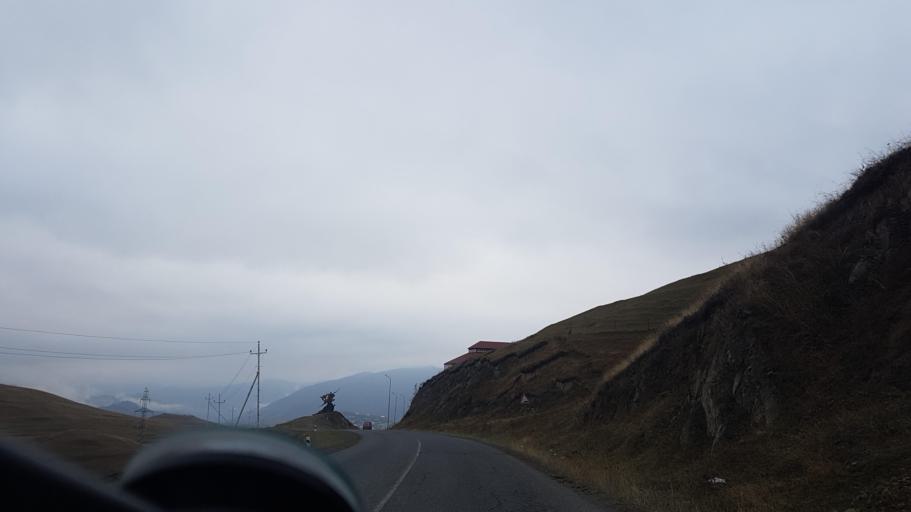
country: AZ
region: Gadabay Rayon
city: Ariqdam
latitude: 40.6151
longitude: 45.8107
